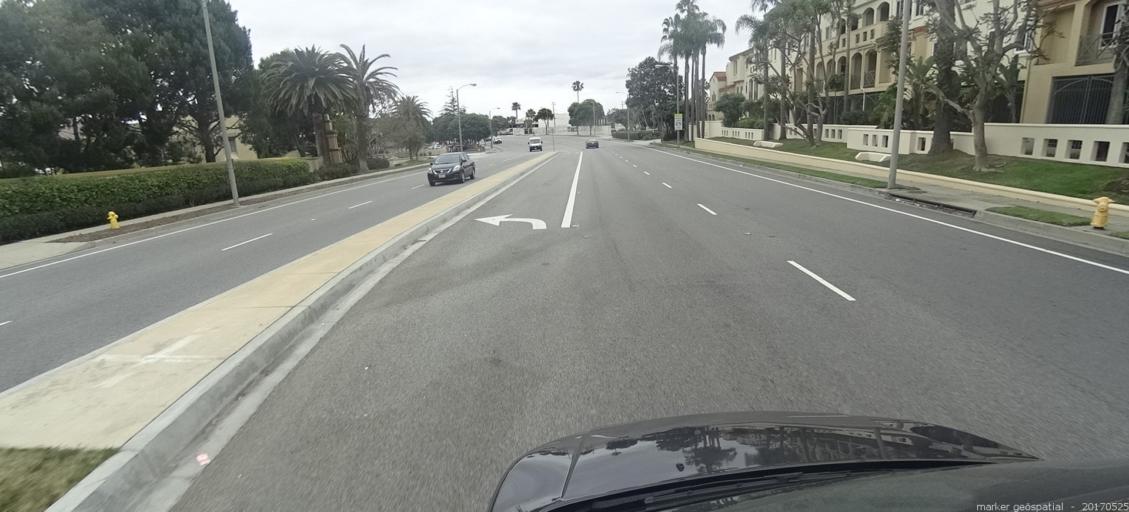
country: US
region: California
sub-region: Los Angeles County
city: Redondo Beach
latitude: 33.8384
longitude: -118.3740
